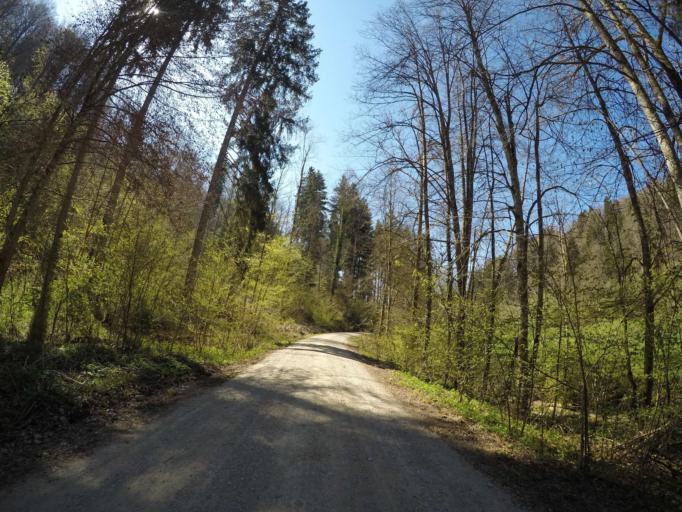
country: DE
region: Baden-Wuerttemberg
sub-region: Tuebingen Region
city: Horgenzell
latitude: 47.7991
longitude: 9.4603
